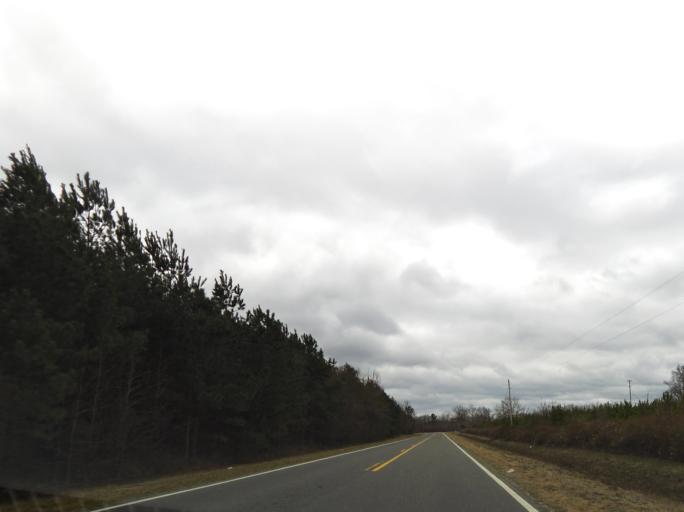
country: US
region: Georgia
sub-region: Bleckley County
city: Cochran
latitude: 32.4667
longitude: -83.3798
